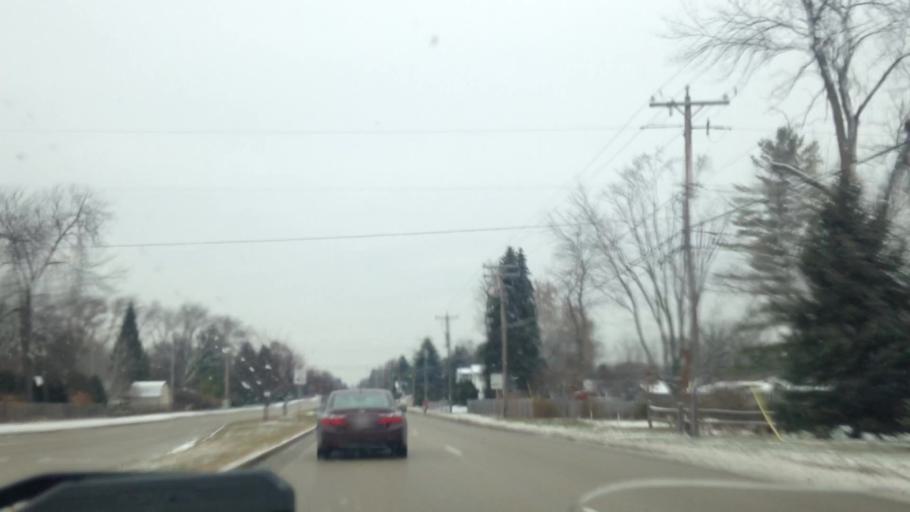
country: US
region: Wisconsin
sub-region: Waukesha County
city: Butler
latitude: 43.1091
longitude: -88.1056
